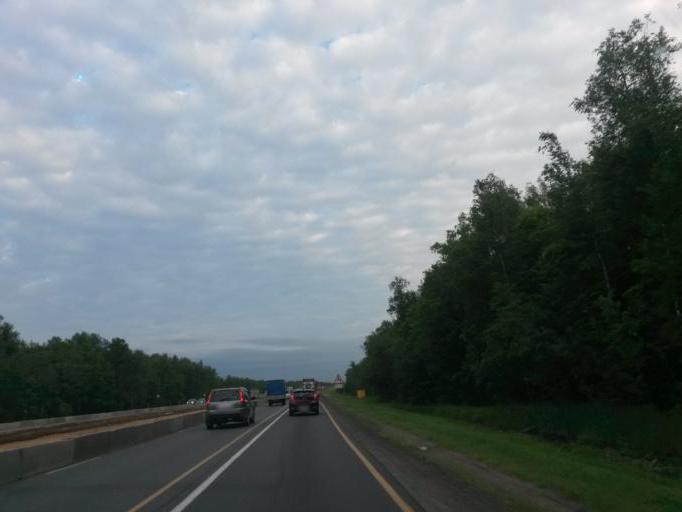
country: RU
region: Moskovskaya
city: Lyubuchany
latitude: 55.2171
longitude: 37.5337
